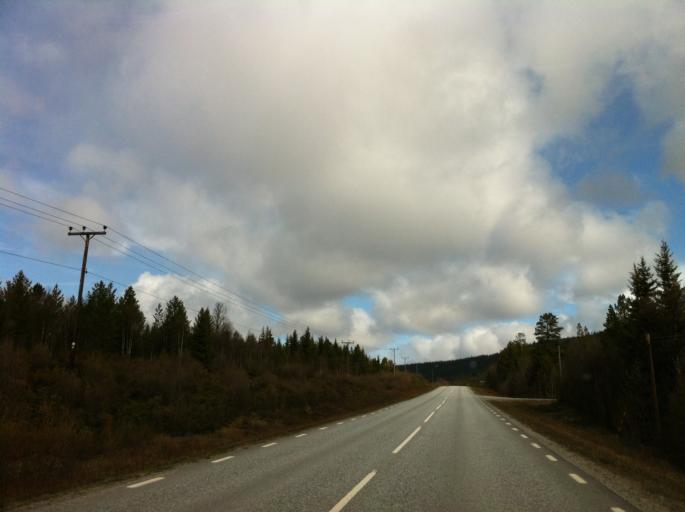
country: SE
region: Jaemtland
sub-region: Are Kommun
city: Are
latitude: 62.5608
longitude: 12.5663
